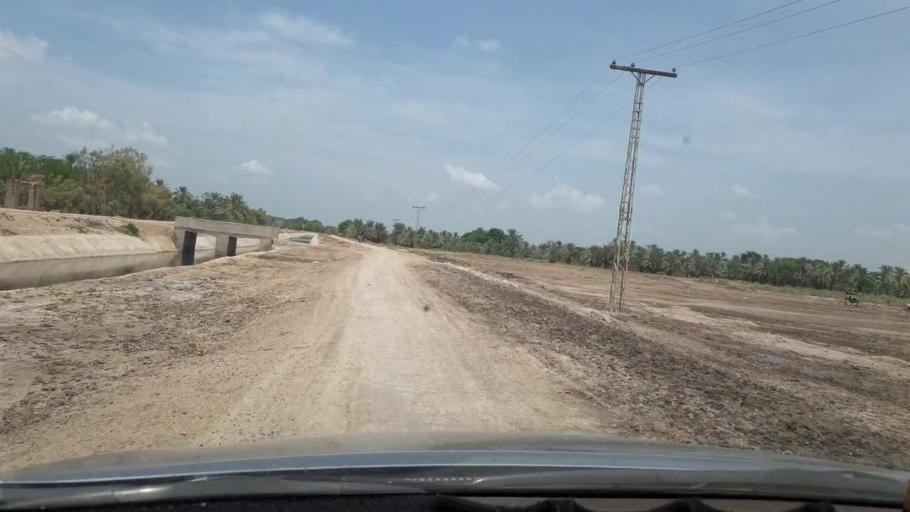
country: PK
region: Sindh
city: Khairpur
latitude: 27.4356
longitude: 68.7818
